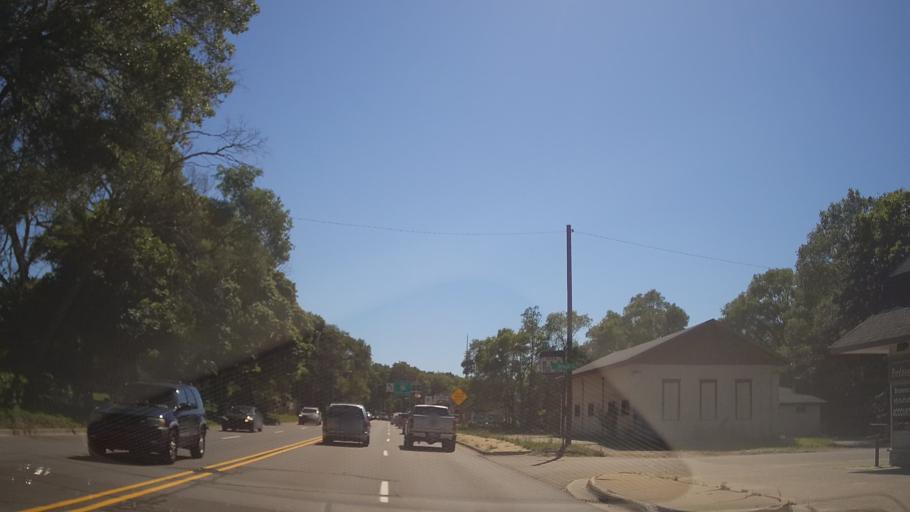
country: US
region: Michigan
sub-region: Emmet County
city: Petoskey
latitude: 45.3879
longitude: -84.9220
